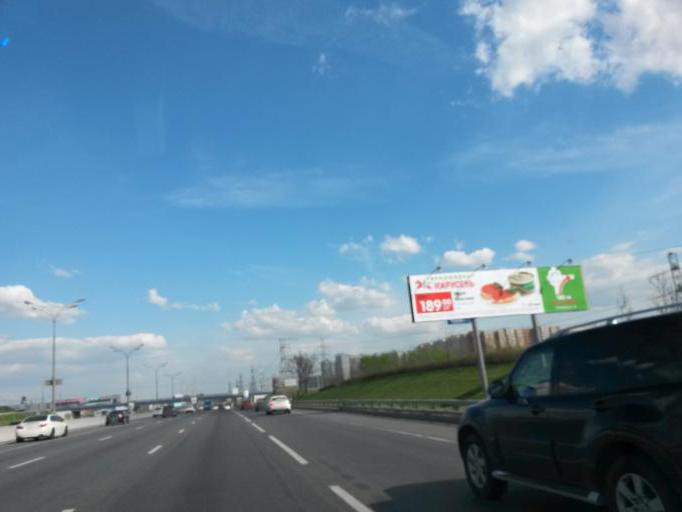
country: RU
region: Moscow
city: Chertanovo Yuzhnoye
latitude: 55.5821
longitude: 37.5678
